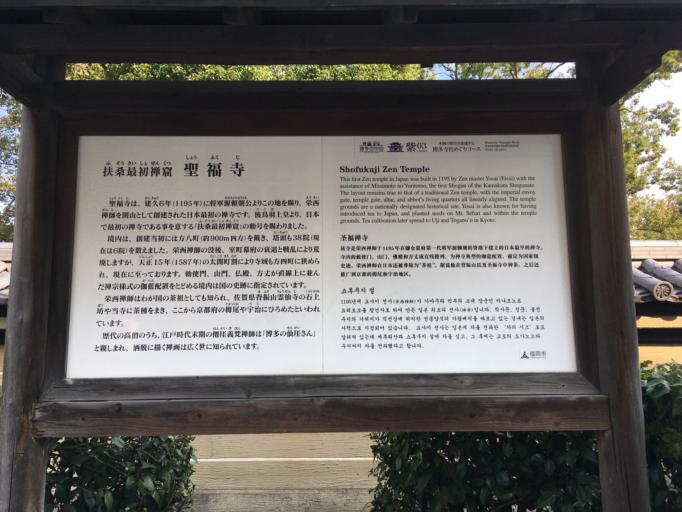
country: JP
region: Fukuoka
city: Fukuoka-shi
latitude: 33.5962
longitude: 130.4136
